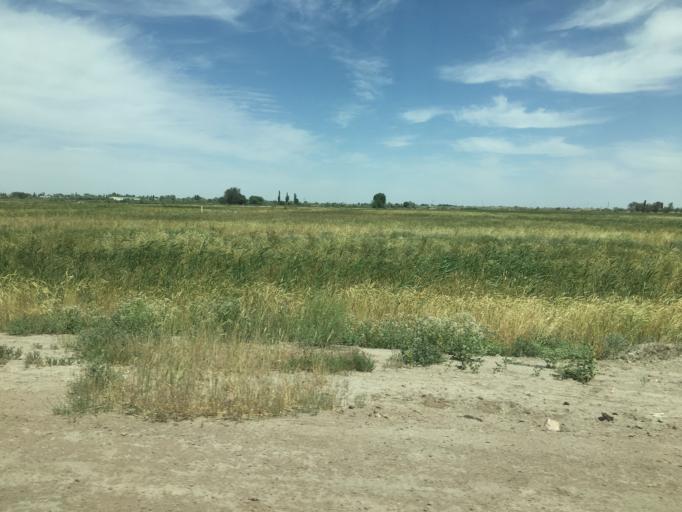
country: TM
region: Dasoguz
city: Dasoguz
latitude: 41.7599
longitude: 59.9545
